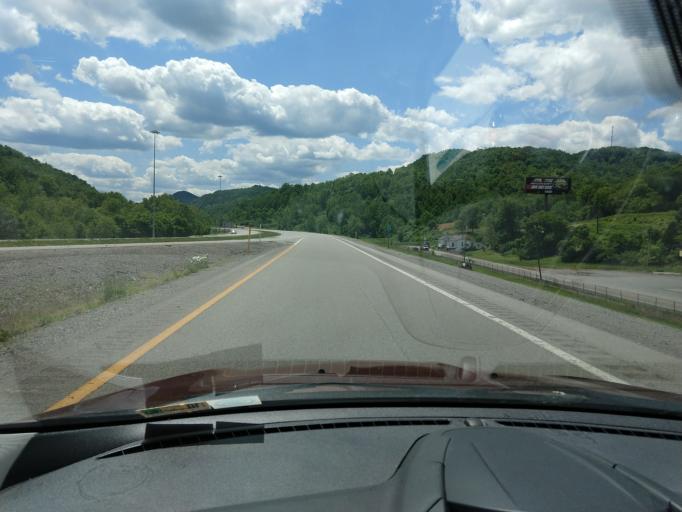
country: US
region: West Virginia
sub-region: Gilmer County
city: Glenville
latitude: 38.8567
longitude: -80.6621
